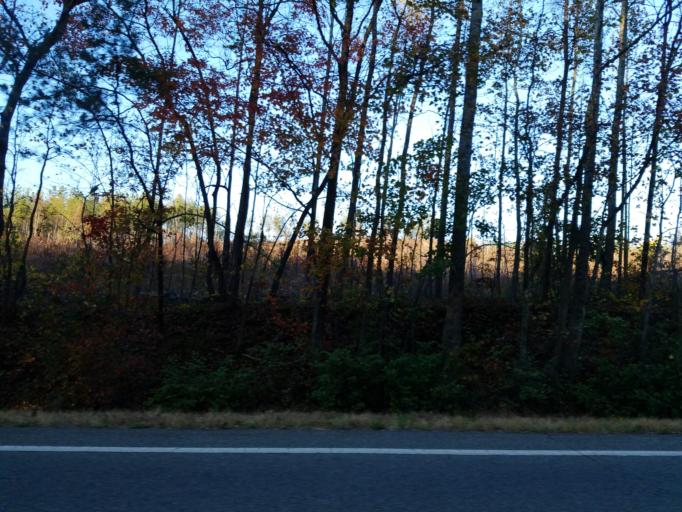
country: US
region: Georgia
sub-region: Dawson County
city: Dawsonville
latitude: 34.5358
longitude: -84.1945
